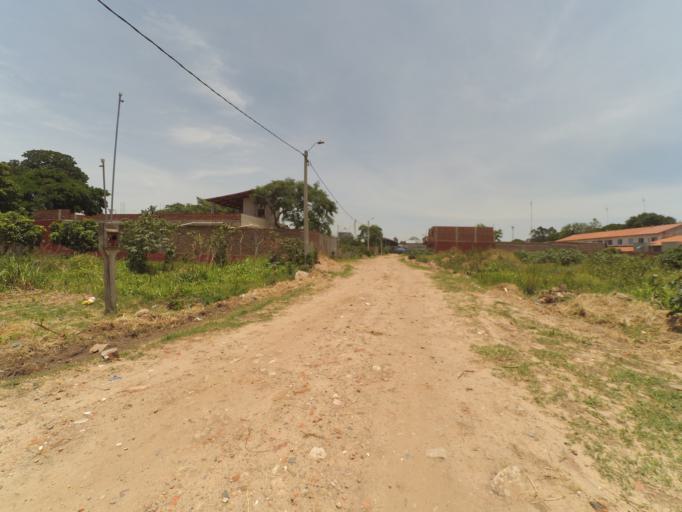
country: BO
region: Santa Cruz
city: Santa Cruz de la Sierra
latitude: -17.8381
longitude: -63.2431
